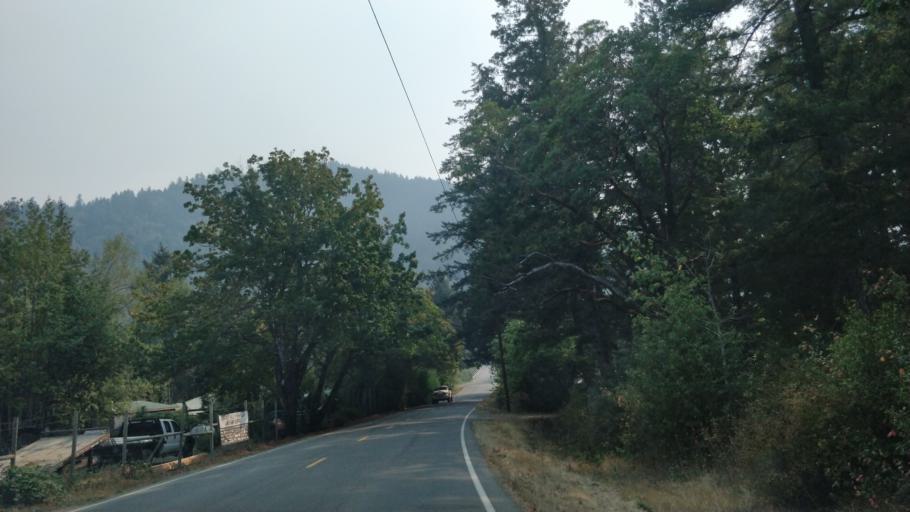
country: US
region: California
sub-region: Humboldt County
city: Rio Dell
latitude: 40.3163
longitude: -124.2833
